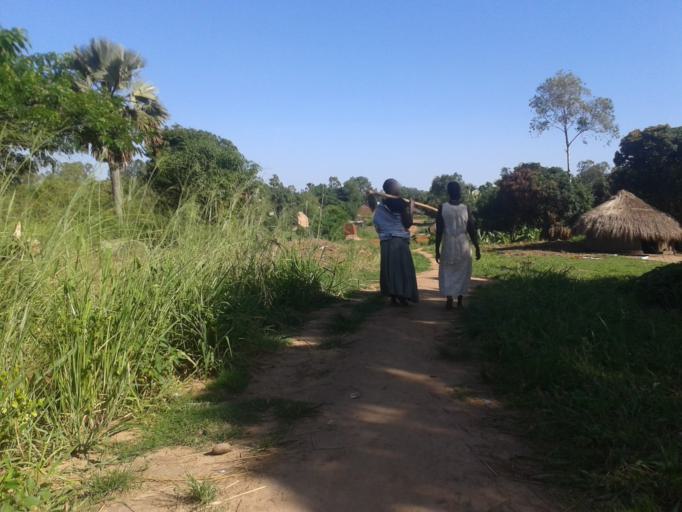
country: UG
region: Northern Region
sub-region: Gulu District
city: Gulu
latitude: 2.7912
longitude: 32.3102
